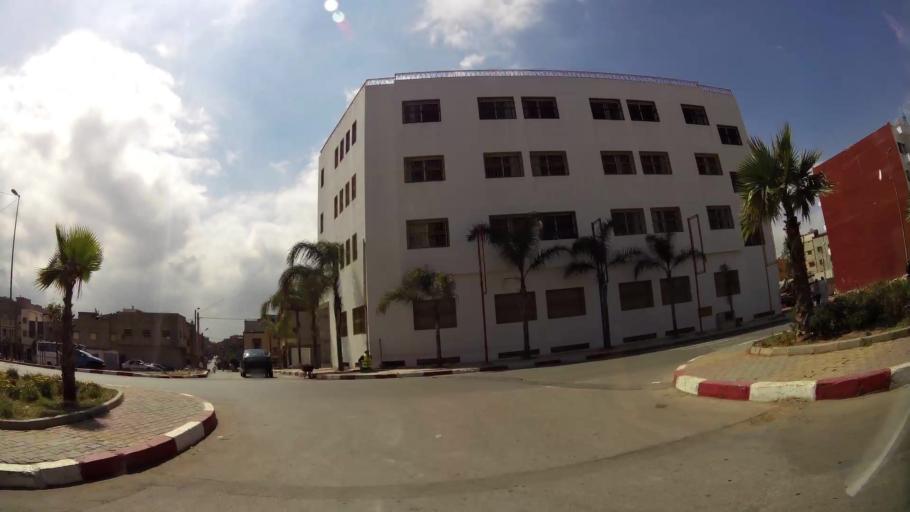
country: MA
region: Rabat-Sale-Zemmour-Zaer
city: Sale
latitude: 34.0702
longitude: -6.7749
